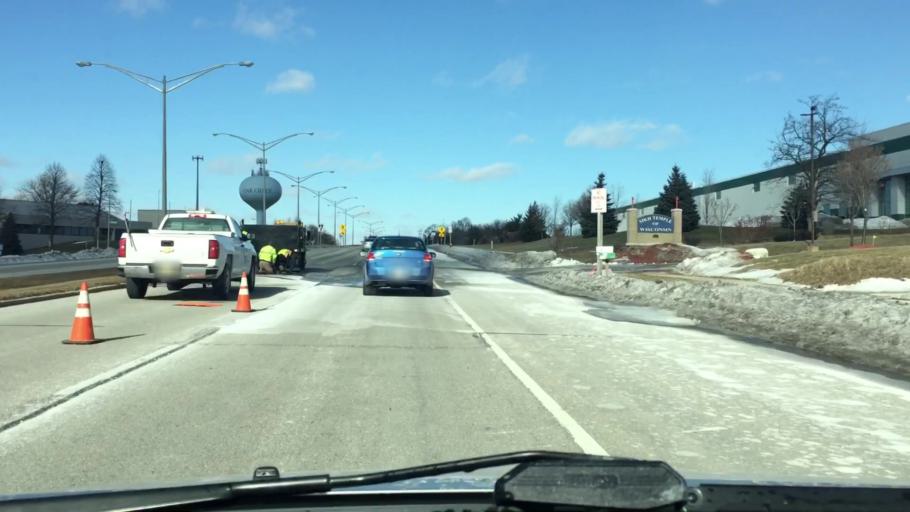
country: US
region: Wisconsin
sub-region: Milwaukee County
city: South Milwaukee
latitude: 42.9079
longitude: -87.9111
